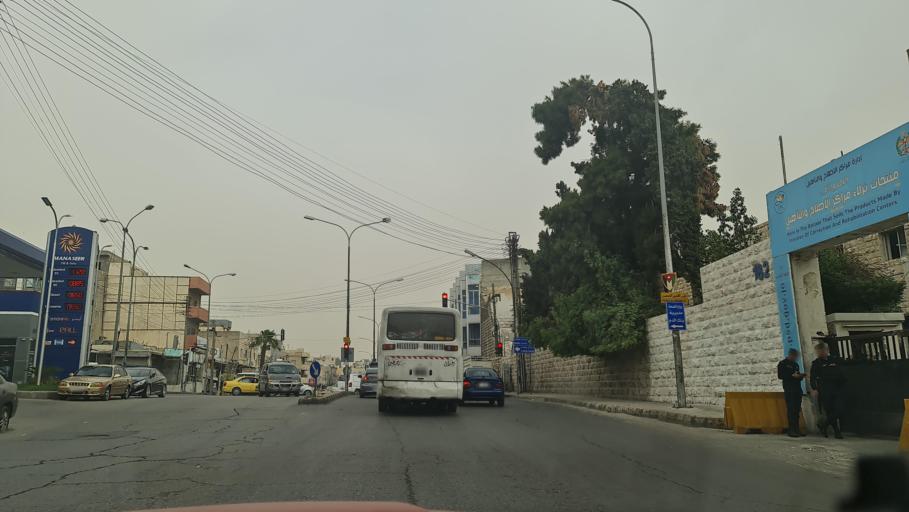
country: JO
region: Amman
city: Al Quwaysimah
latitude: 31.9331
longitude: 35.9336
